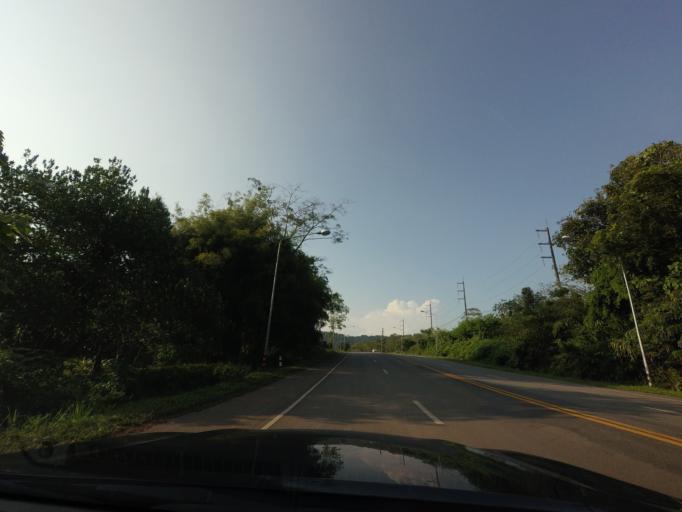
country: TH
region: Loei
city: Dan Sai
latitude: 17.2110
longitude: 101.1531
